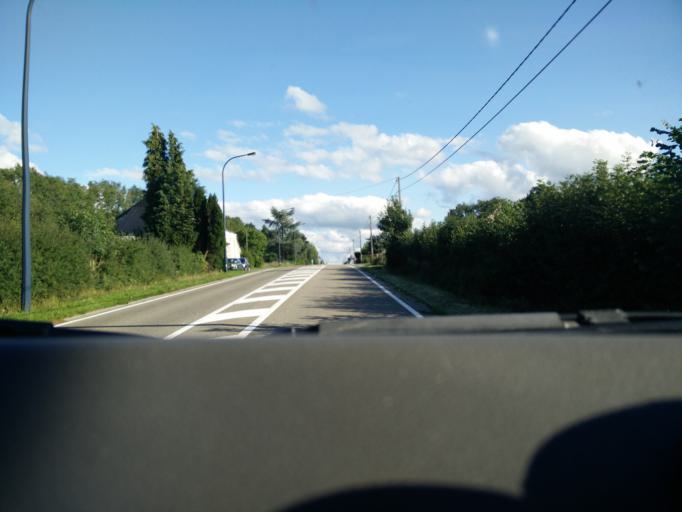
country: BE
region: Wallonia
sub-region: Province du Hainaut
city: Beaumont
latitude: 50.1841
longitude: 4.2208
